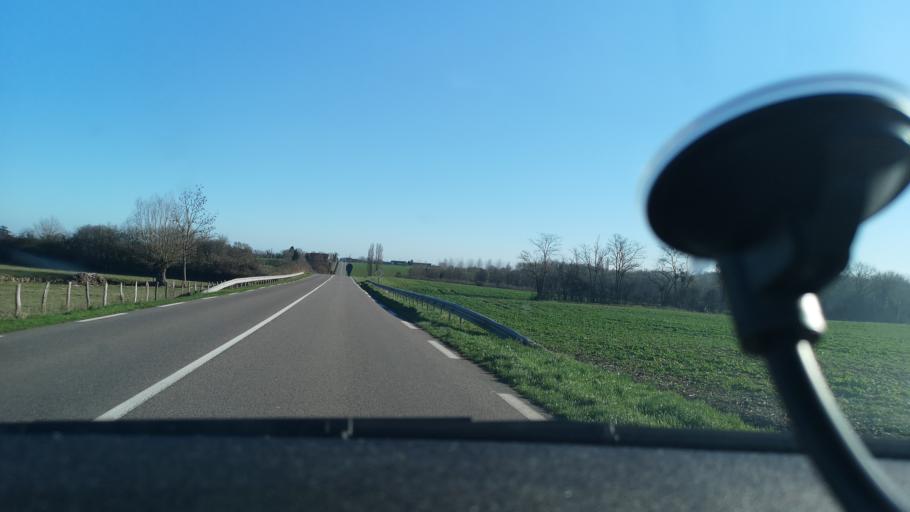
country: FR
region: Bourgogne
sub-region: Departement de Saone-et-Loire
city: Saint-Martin-en-Bresse
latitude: 46.7501
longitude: 5.0385
